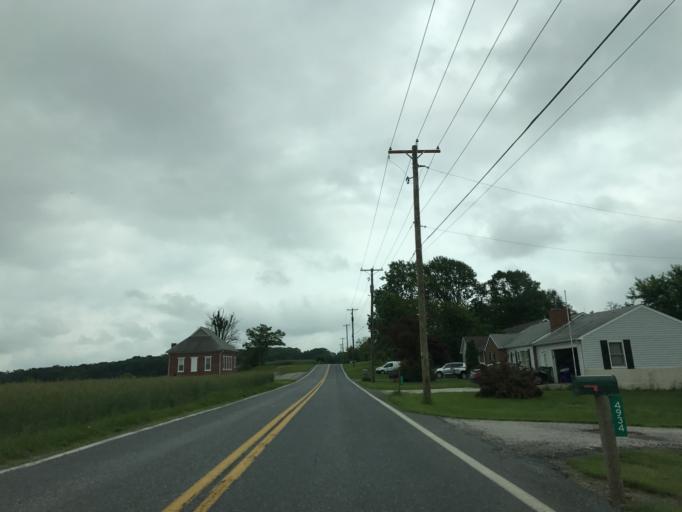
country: US
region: Pennsylvania
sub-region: York County
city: Dallastown
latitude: 39.8437
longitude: -76.6357
